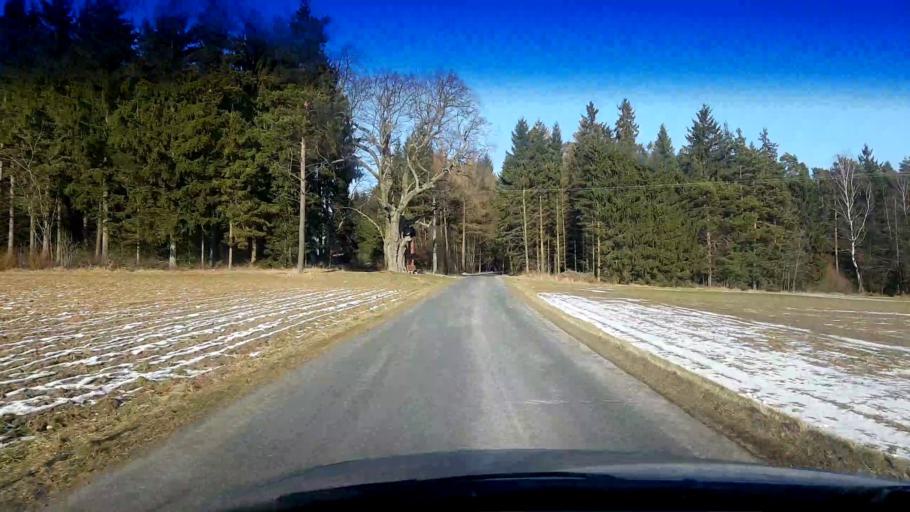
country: DE
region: Bavaria
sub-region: Upper Palatinate
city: Waldsassen
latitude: 50.0443
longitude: 12.2879
